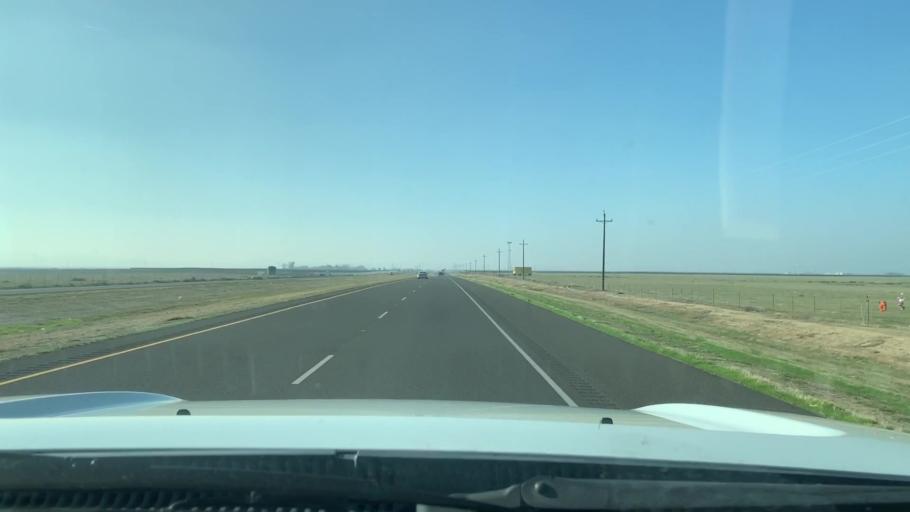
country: US
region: California
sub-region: Kern County
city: Lost Hills
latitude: 35.6155
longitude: -119.8373
